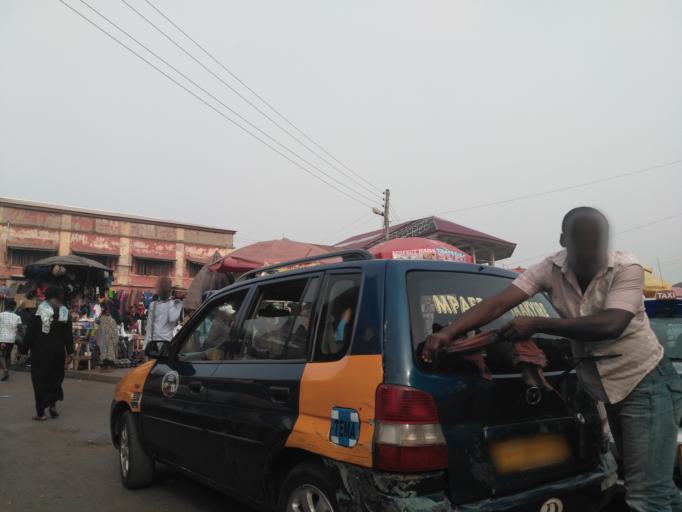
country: GH
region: Ashanti
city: Kumasi
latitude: 6.6963
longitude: -1.6215
